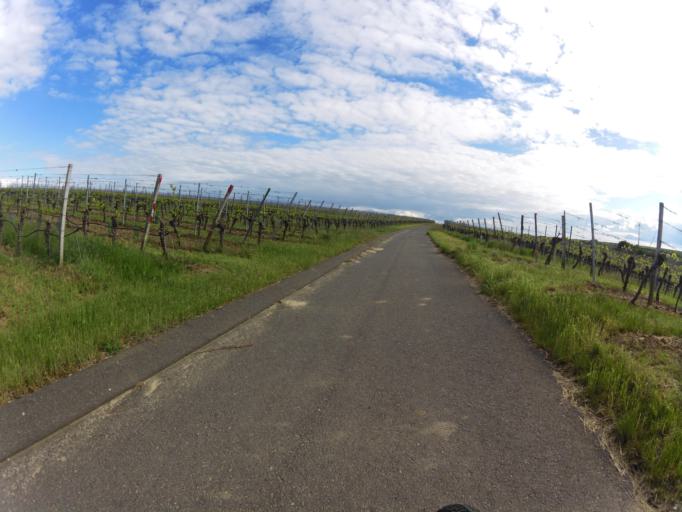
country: DE
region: Bavaria
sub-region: Regierungsbezirk Unterfranken
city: Nordheim
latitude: 49.8463
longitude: 10.1856
